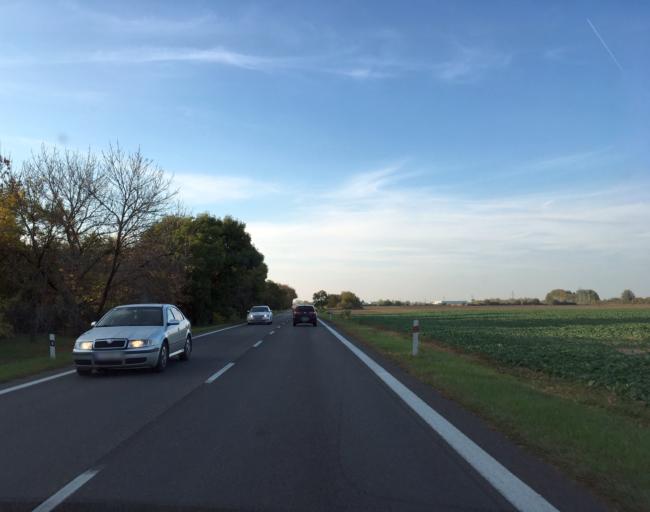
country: SK
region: Nitriansky
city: Sellye
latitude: 48.1554
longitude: 17.9143
